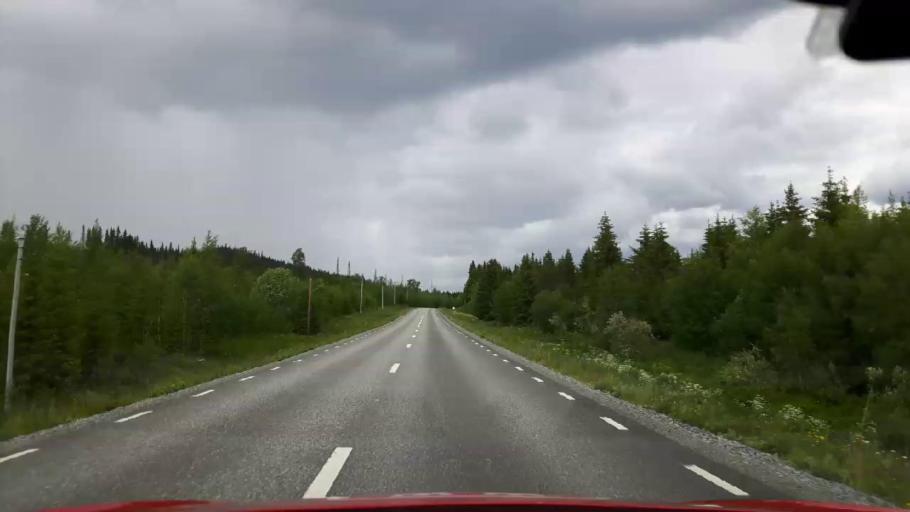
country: SE
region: Jaemtland
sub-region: Krokoms Kommun
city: Krokom
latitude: 63.6903
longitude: 14.3225
